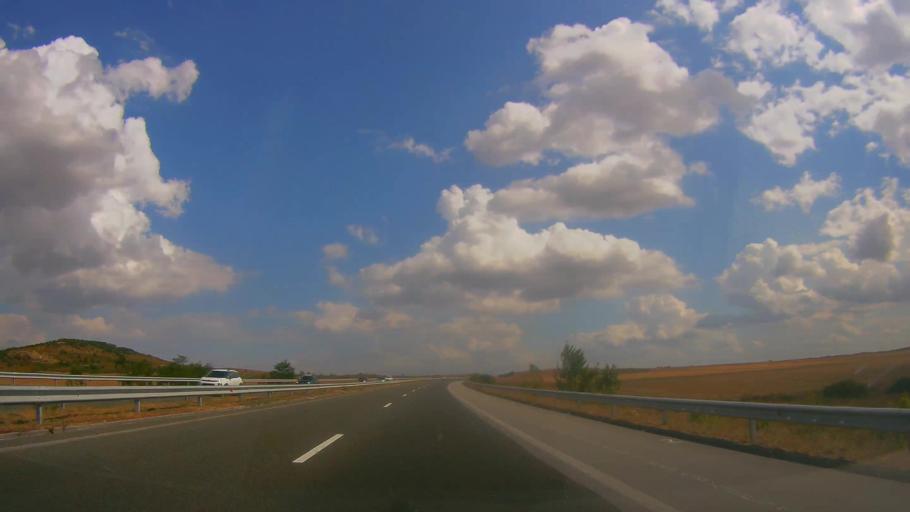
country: BG
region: Yambol
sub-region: Obshtina Yambol
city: Yambol
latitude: 42.5443
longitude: 26.4567
